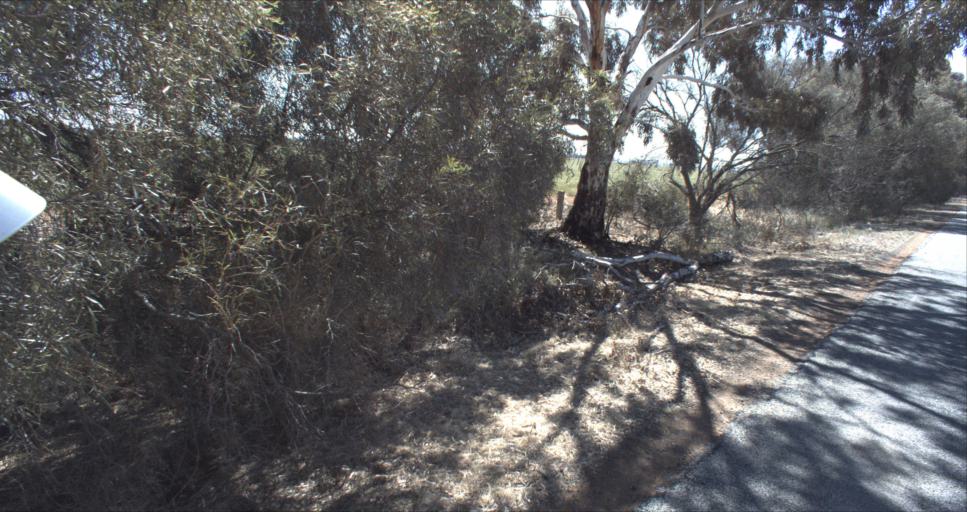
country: AU
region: New South Wales
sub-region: Leeton
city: Leeton
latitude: -34.5778
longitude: 146.2640
